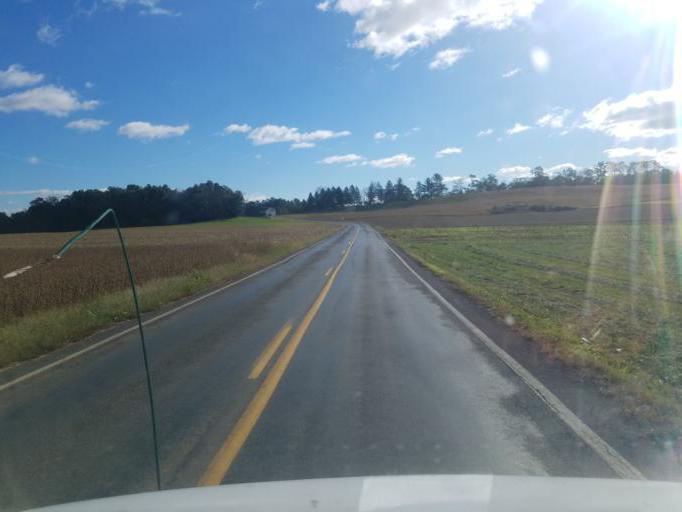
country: US
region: Pennsylvania
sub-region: Franklin County
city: Guilford Siding
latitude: 39.8094
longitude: -77.6423
